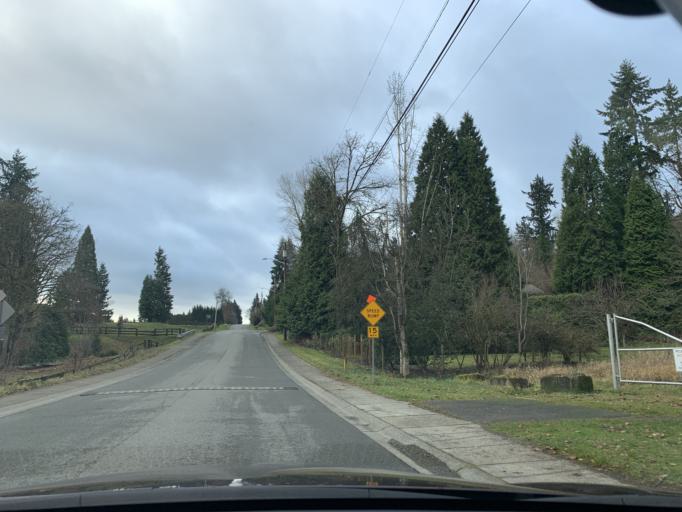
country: US
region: Washington
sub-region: King County
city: Woodinville
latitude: 47.7366
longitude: -122.1637
